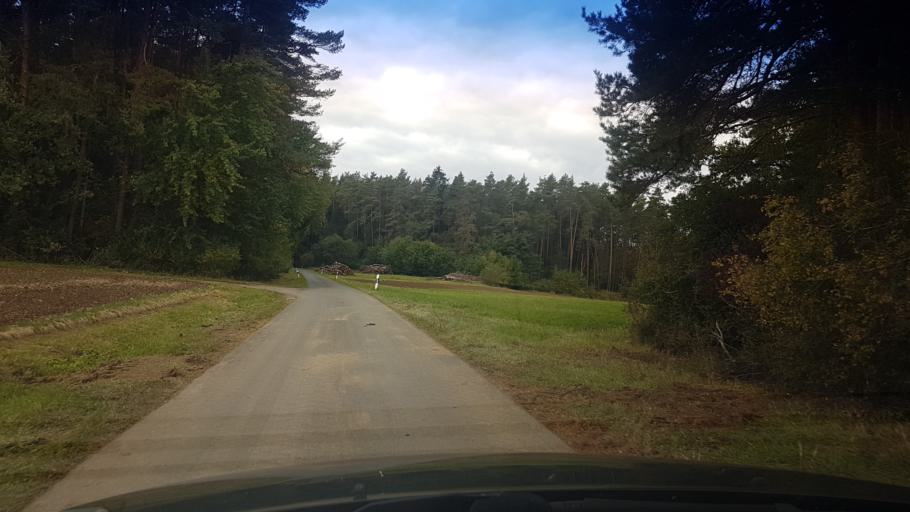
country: DE
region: Bavaria
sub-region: Upper Franconia
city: Stadelhofen
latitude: 50.0050
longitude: 11.2299
